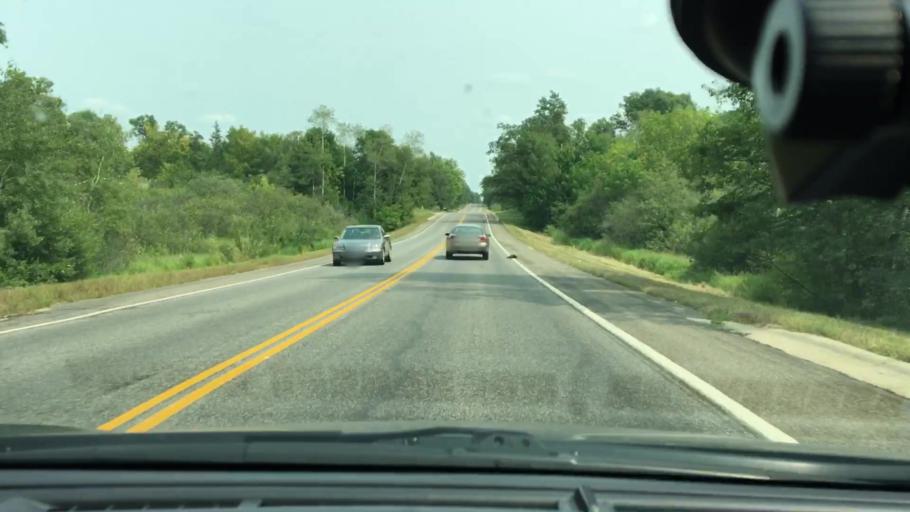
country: US
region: Minnesota
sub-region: Cass County
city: East Gull Lake
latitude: 46.4128
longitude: -94.3227
